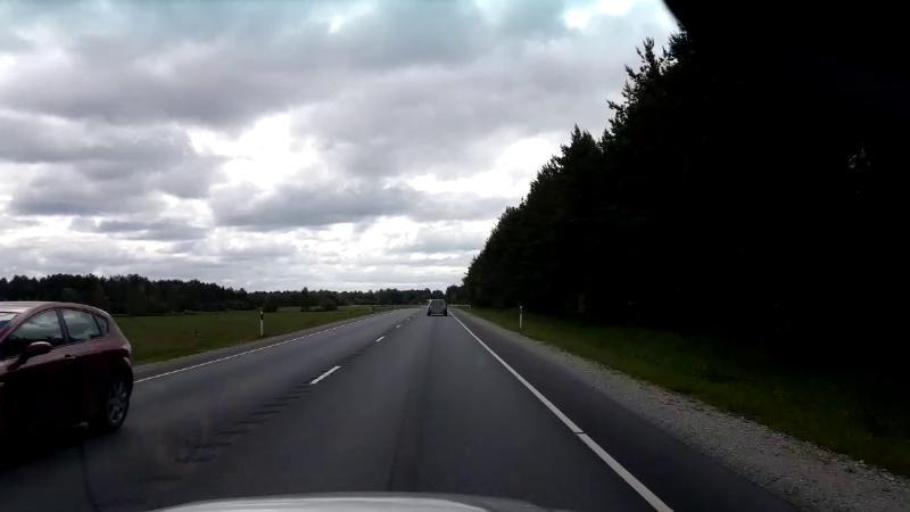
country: EE
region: Paernumaa
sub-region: Halinga vald
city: Parnu-Jaagupi
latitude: 58.6621
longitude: 24.4653
